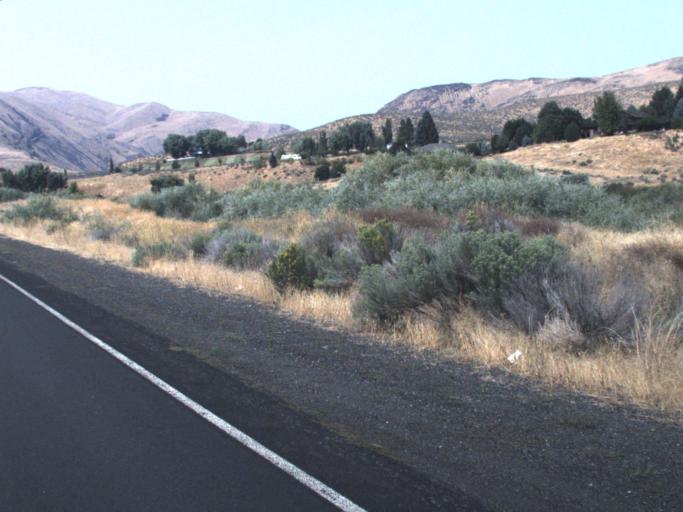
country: US
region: Washington
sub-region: Yakima County
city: Selah
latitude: 46.7733
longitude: -120.4492
